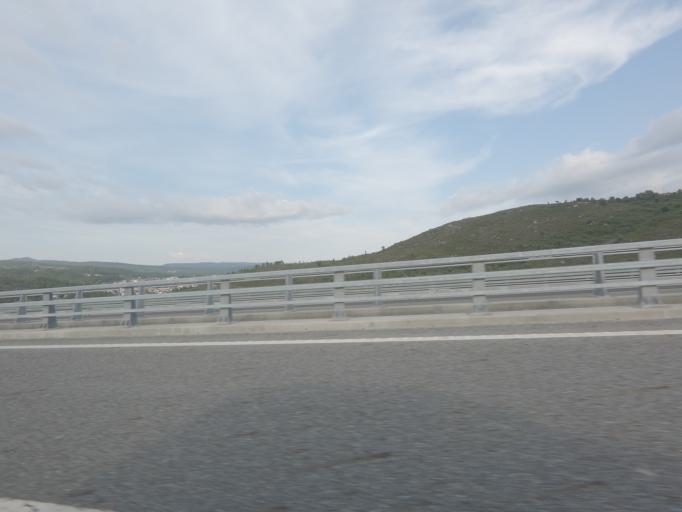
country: PT
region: Vila Real
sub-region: Boticas
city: Boticas
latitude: 41.6389
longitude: -7.5925
